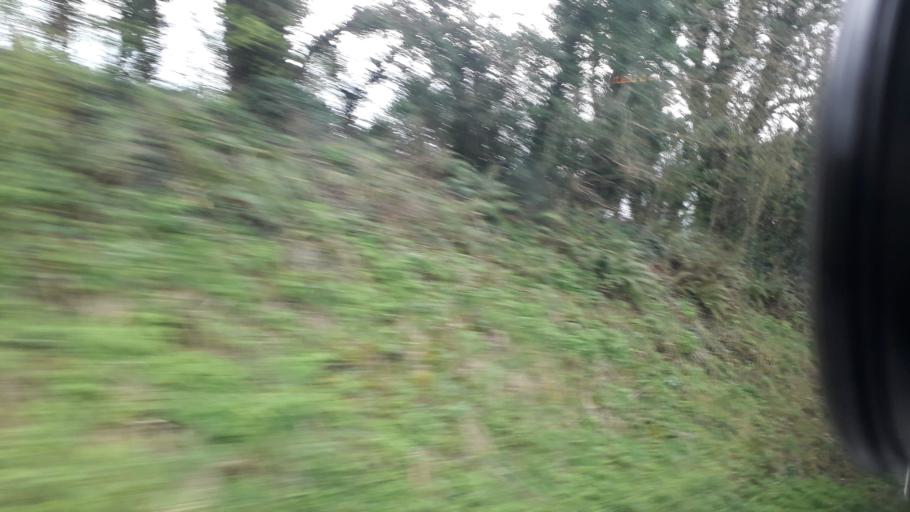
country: IE
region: Leinster
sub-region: An Longfort
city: Longford
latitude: 53.7259
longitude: -7.7754
